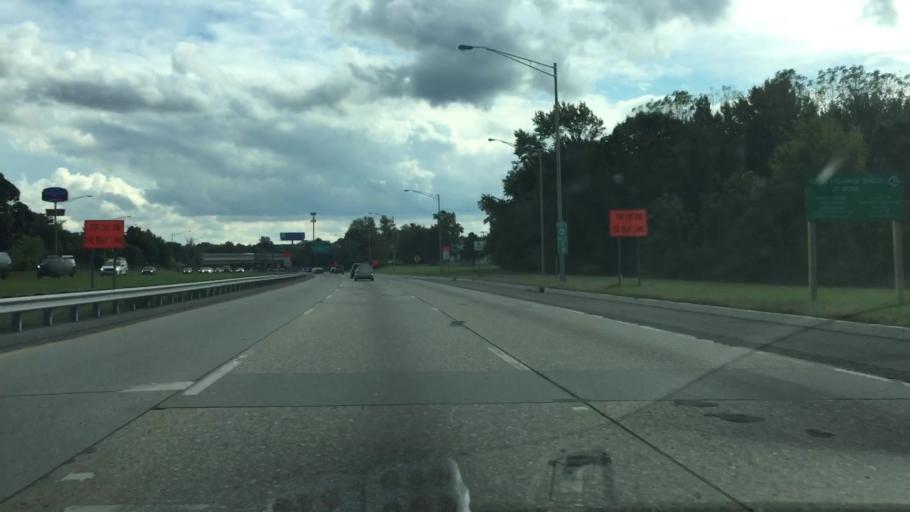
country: US
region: New Jersey
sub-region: Camden County
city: Glendora
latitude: 39.8353
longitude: -75.0915
